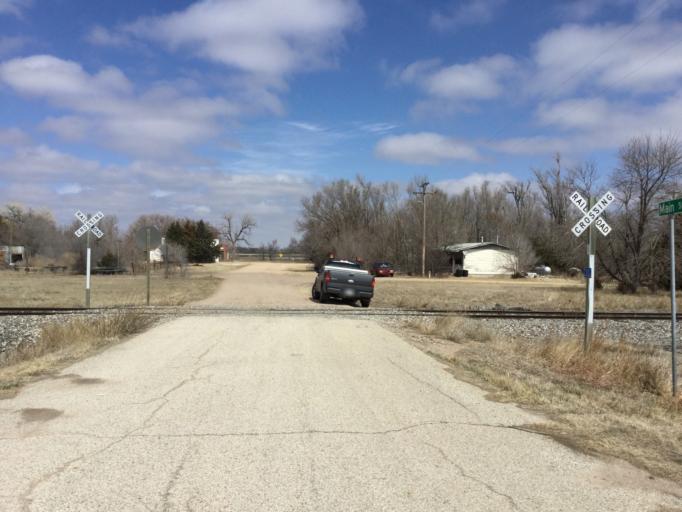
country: US
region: Kansas
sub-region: Barton County
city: Great Bend
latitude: 38.4214
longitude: -98.8891
